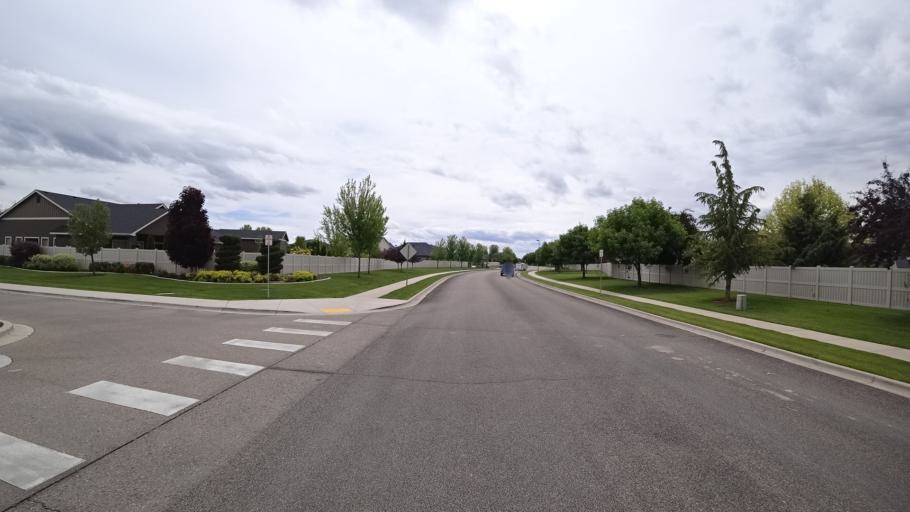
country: US
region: Idaho
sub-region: Ada County
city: Meridian
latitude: 43.6420
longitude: -116.4237
